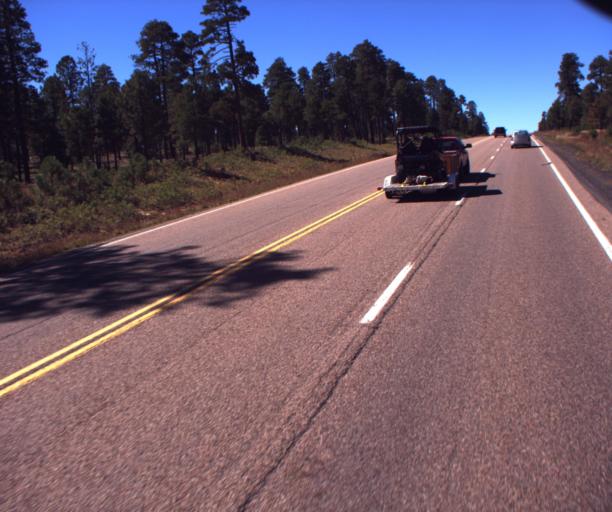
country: US
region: Arizona
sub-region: Navajo County
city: Heber-Overgaard
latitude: 34.3351
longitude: -110.7470
